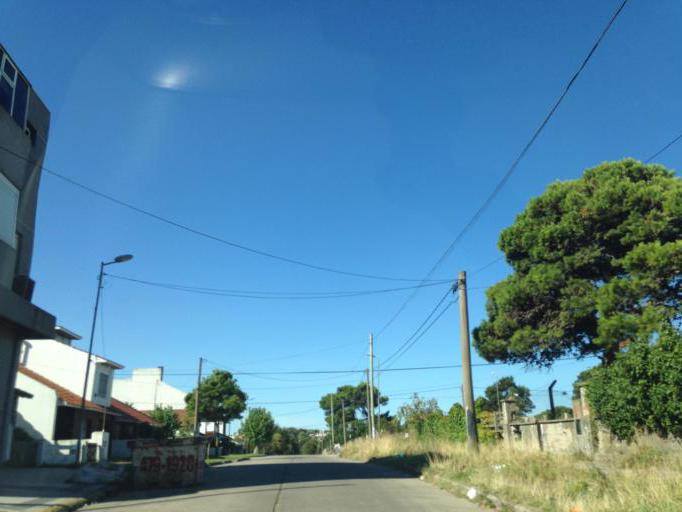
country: AR
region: Buenos Aires
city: Mar del Plata
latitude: -38.0347
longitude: -57.5500
